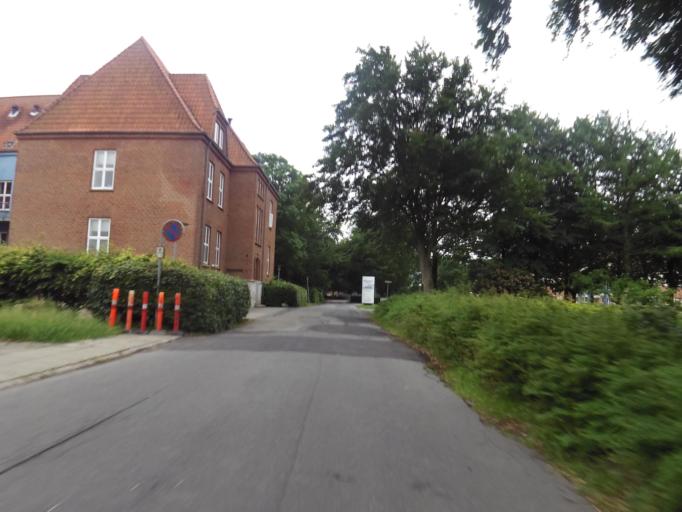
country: DK
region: South Denmark
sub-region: Esbjerg Kommune
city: Ribe
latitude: 55.3258
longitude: 8.7738
